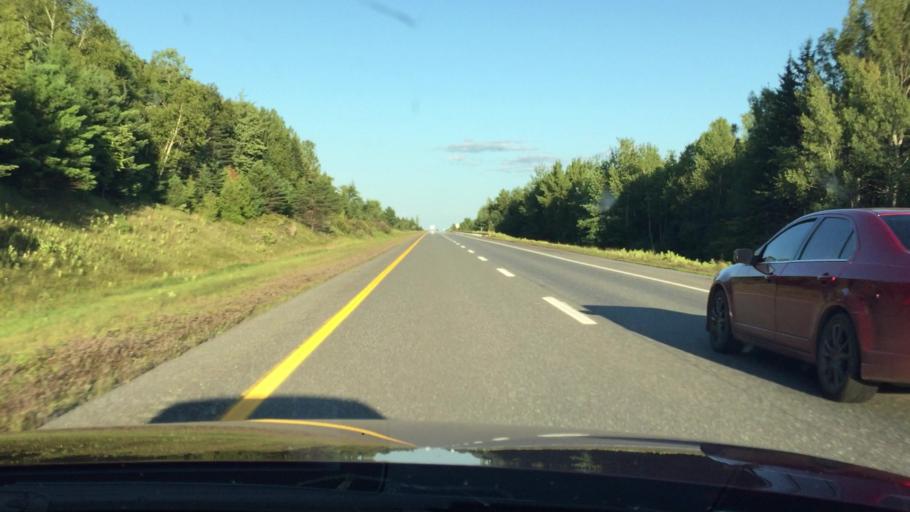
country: US
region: Maine
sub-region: Aroostook County
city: Hodgdon
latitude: 46.1445
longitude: -68.0509
